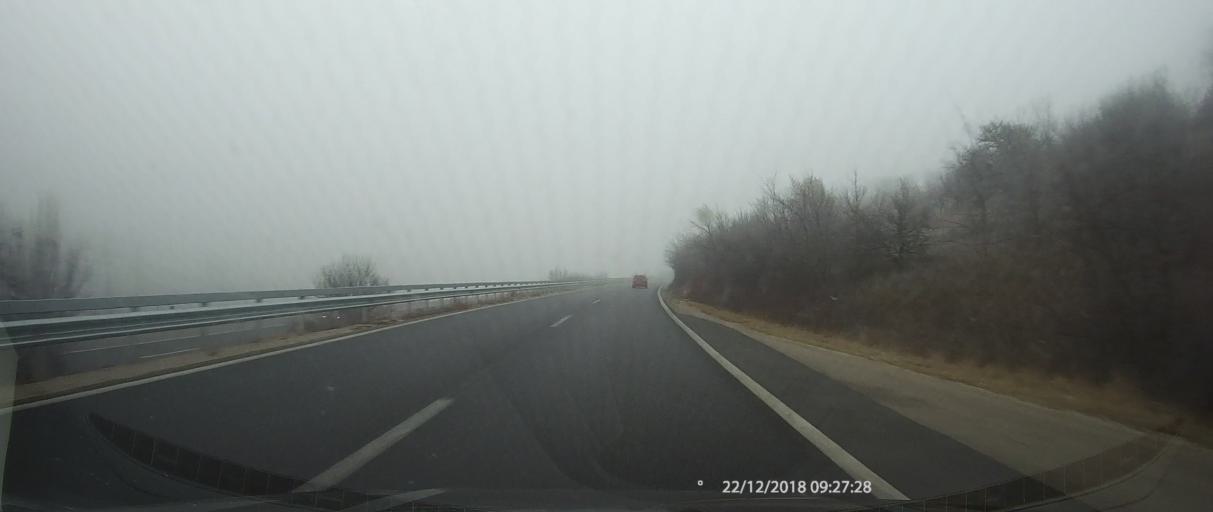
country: MK
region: Kumanovo
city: Romanovce
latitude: 42.0496
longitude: 21.6838
